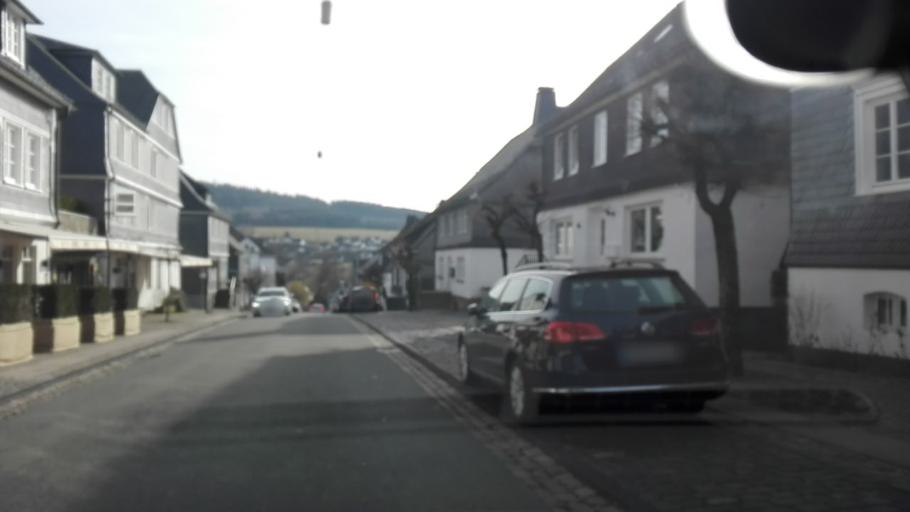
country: DE
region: North Rhine-Westphalia
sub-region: Regierungsbezirk Arnsberg
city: Schmallenberg
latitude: 51.1471
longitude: 8.2846
